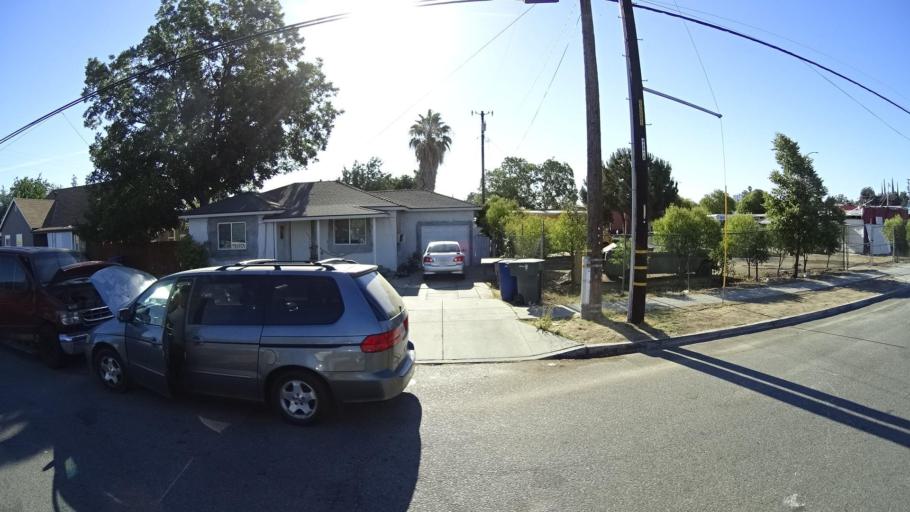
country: US
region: California
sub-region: Fresno County
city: Fresno
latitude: 36.7511
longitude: -119.7432
